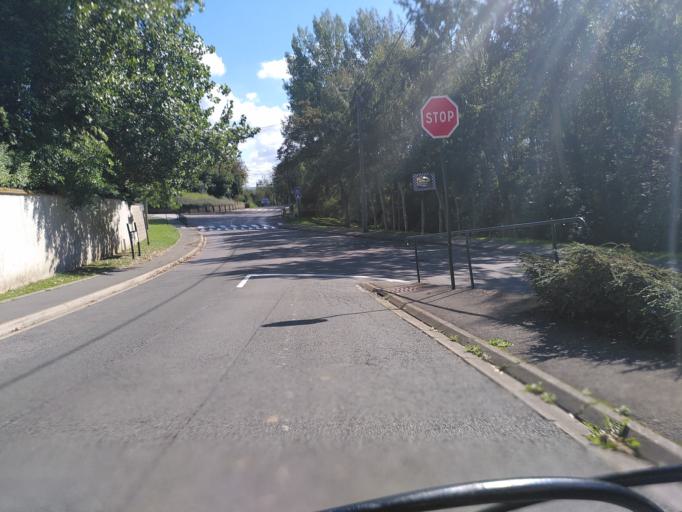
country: FR
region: Nord-Pas-de-Calais
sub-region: Departement du Pas-de-Calais
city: Wimille
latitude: 50.7677
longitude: 1.6300
